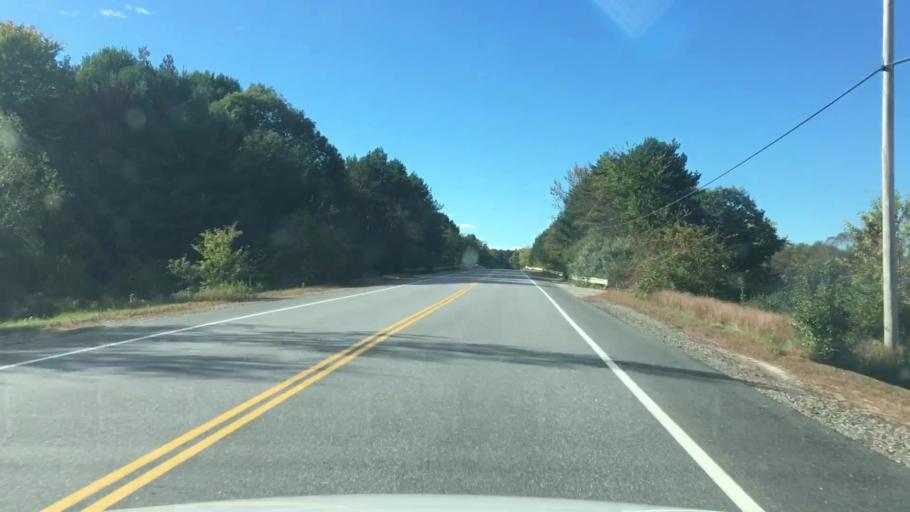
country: US
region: Maine
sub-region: Sagadahoc County
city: Topsham
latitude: 43.9266
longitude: -69.9973
